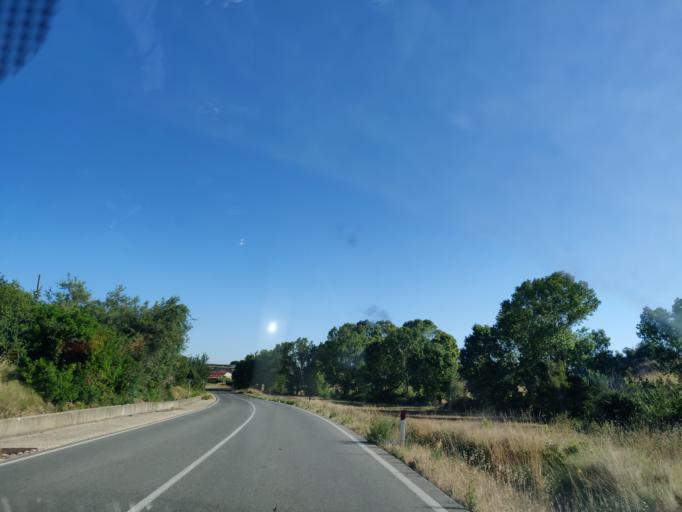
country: IT
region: Latium
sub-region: Citta metropolitana di Roma Capitale
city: Aurelia
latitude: 42.1461
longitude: 11.7890
